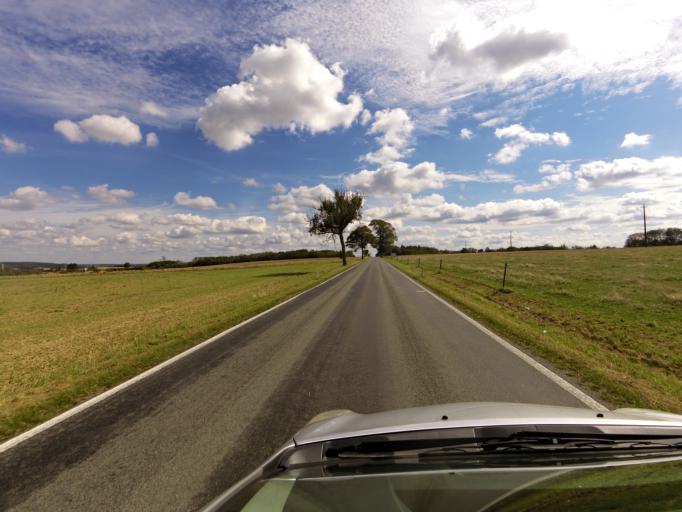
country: BE
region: Wallonia
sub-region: Province de Namur
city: Somme-Leuze
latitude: 50.3538
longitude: 5.3359
